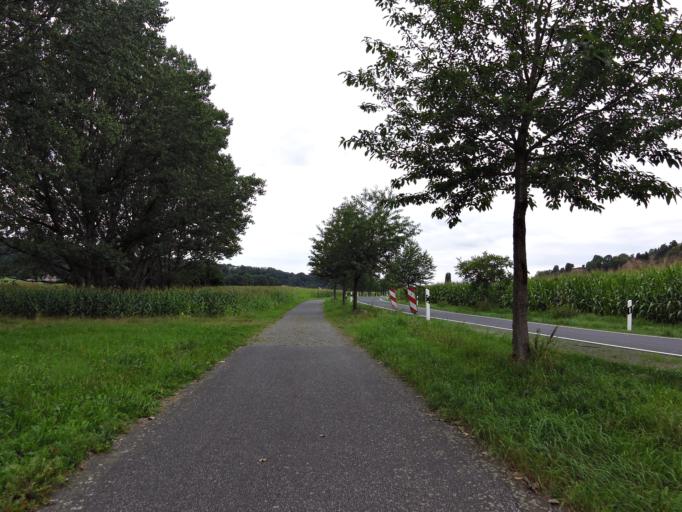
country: DE
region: Saxony
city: Meissen
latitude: 51.1911
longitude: 13.4339
